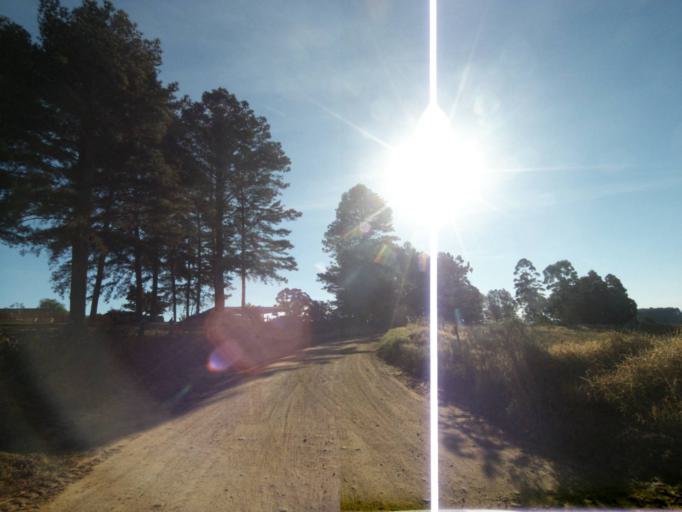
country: BR
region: Parana
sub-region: Tibagi
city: Tibagi
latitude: -24.5477
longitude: -50.6199
